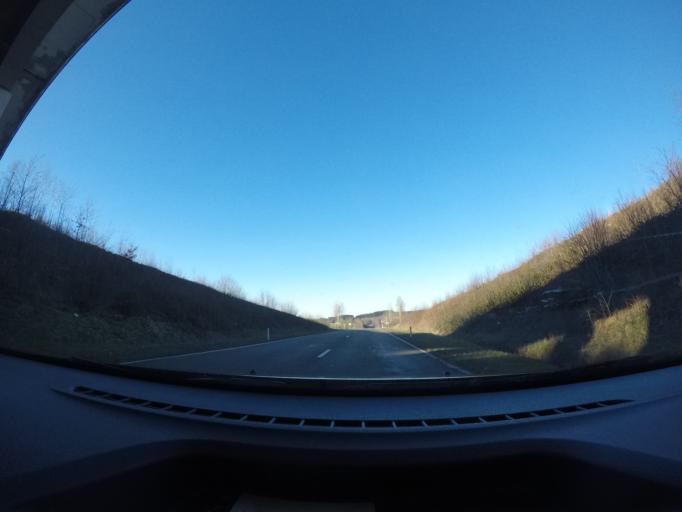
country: BE
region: Wallonia
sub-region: Province du Luxembourg
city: Bertrix
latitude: 49.8533
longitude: 5.2857
